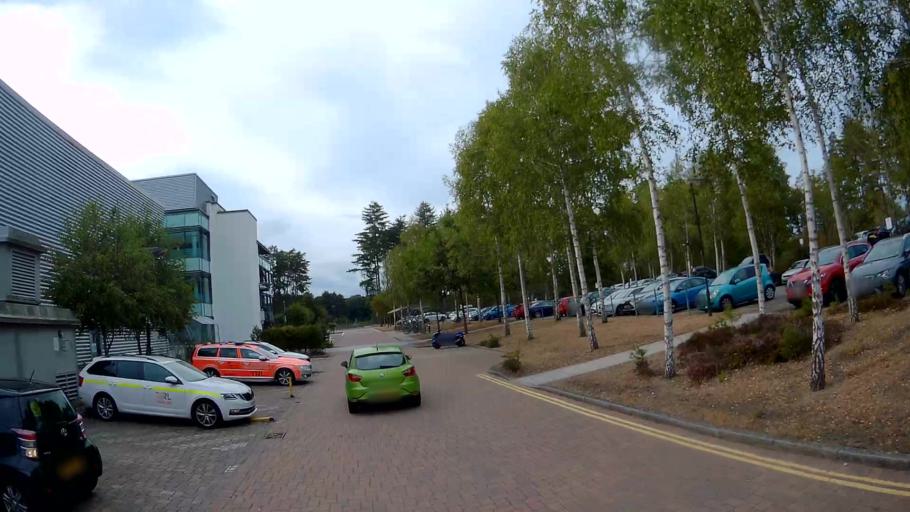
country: GB
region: England
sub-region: Bracknell Forest
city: Crowthorne
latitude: 51.3832
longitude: -0.7829
